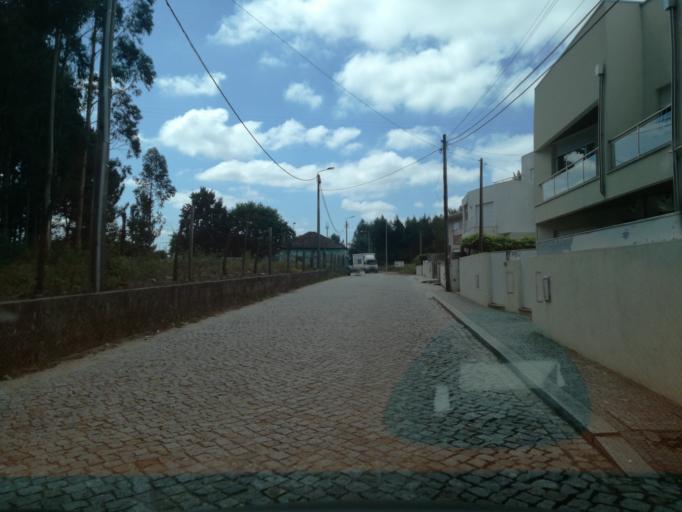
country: PT
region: Porto
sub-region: Maia
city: Nogueira
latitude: 41.2431
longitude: -8.5940
